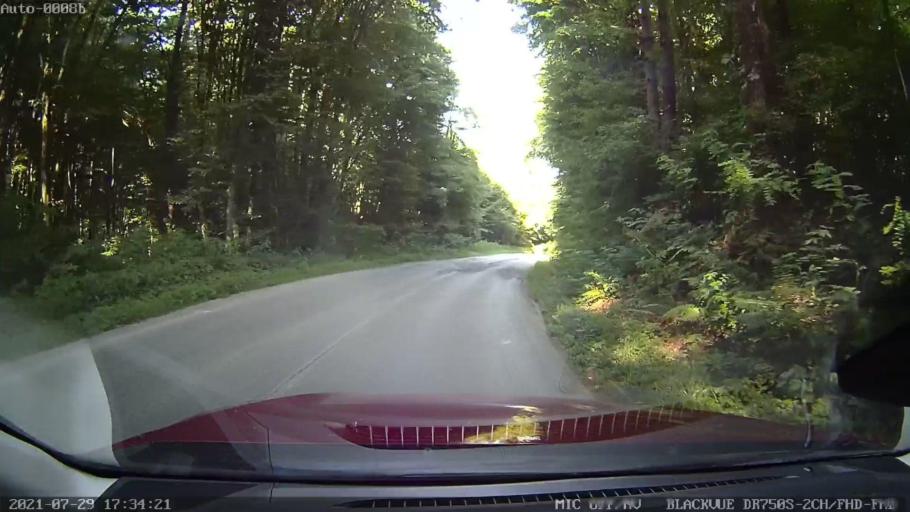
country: HR
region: Varazdinska
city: Vinica
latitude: 46.2939
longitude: 16.1458
